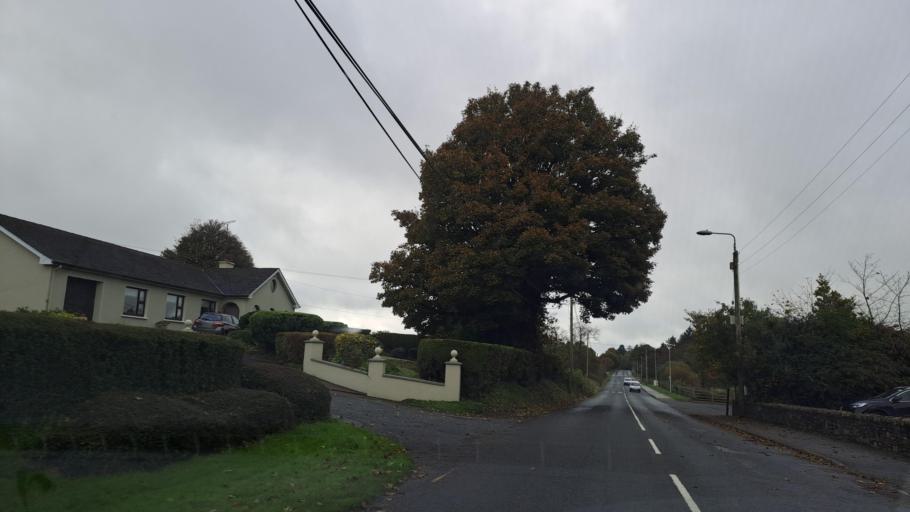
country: IE
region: Ulster
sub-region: An Cabhan
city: Bailieborough
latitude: 53.9124
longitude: -6.9730
